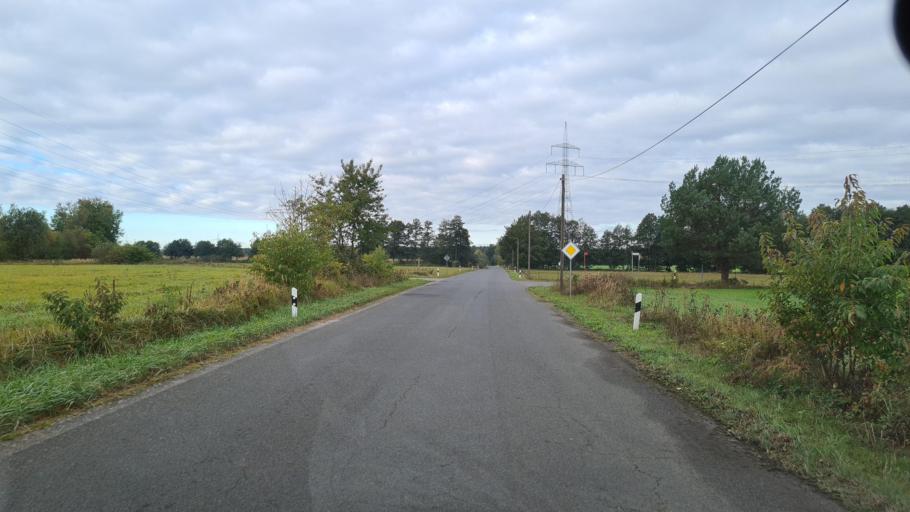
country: DE
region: Brandenburg
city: Altdobern
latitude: 51.6767
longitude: 14.0769
